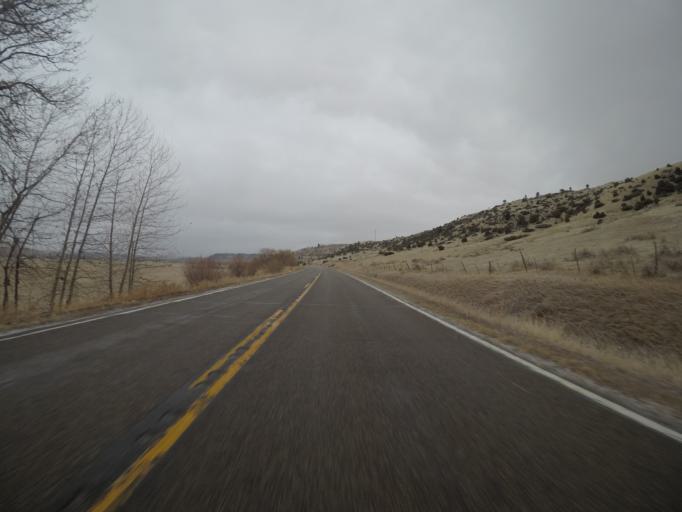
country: US
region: Montana
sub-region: Stillwater County
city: Absarokee
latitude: 45.5217
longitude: -109.4660
